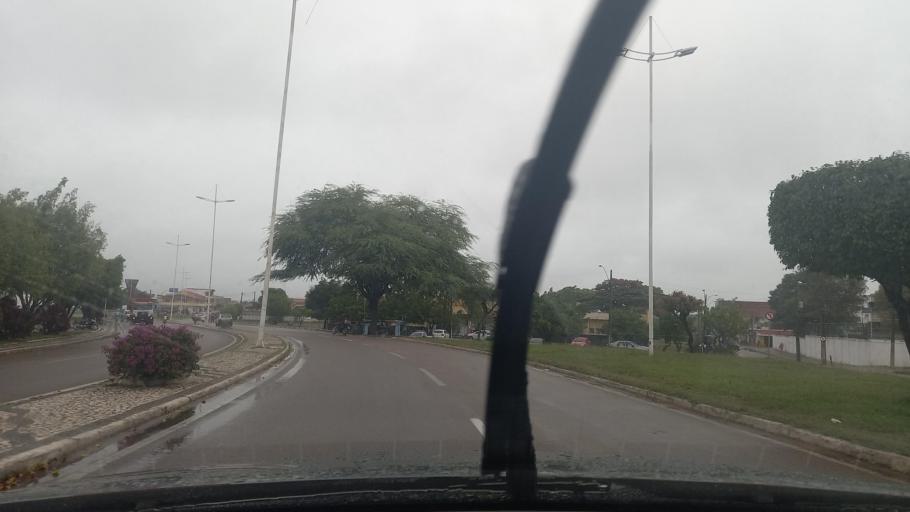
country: BR
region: Bahia
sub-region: Paulo Afonso
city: Paulo Afonso
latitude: -9.3987
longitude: -38.2310
